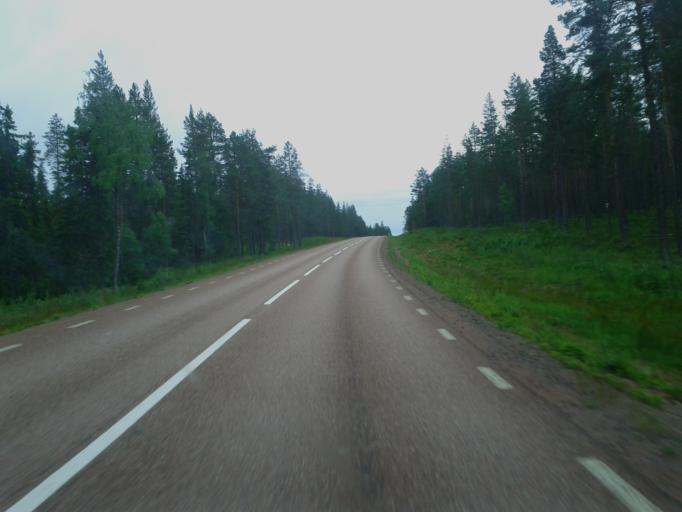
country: SE
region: Dalarna
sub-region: Alvdalens Kommun
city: AElvdalen
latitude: 61.4828
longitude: 13.4233
